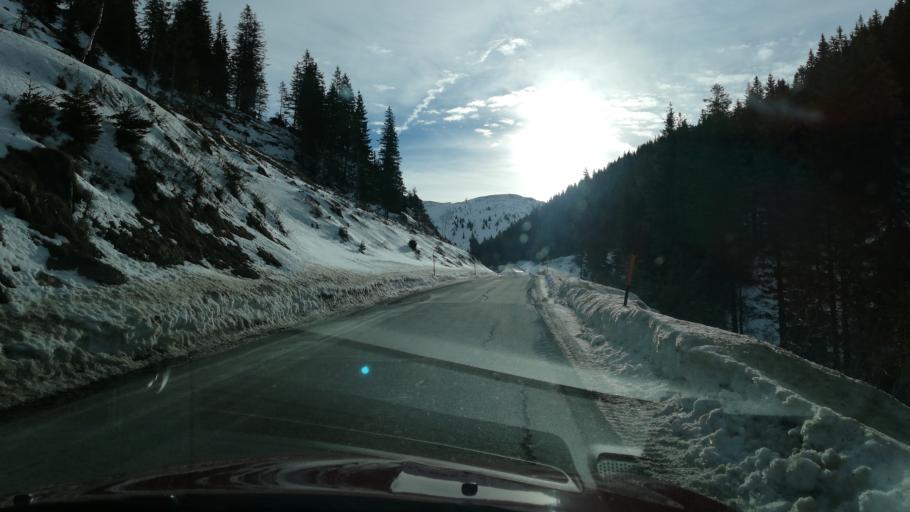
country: AT
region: Styria
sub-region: Politischer Bezirk Liezen
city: Donnersbach
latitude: 47.4101
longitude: 14.1866
